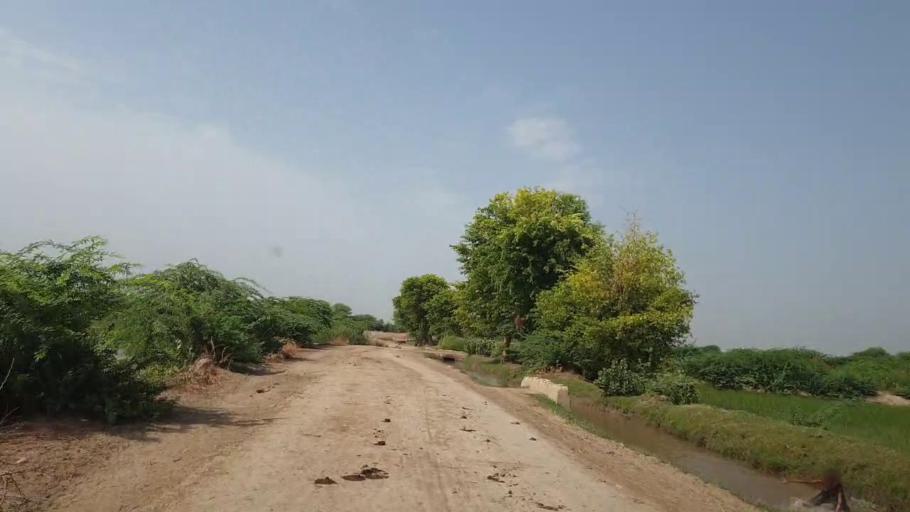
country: PK
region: Sindh
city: Lakhi
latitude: 27.7964
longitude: 68.7102
